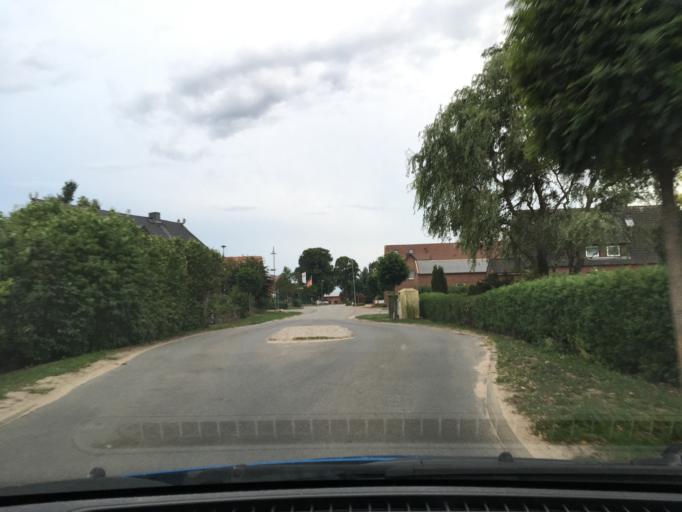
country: DE
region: Schleswig-Holstein
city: Lanze
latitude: 53.3879
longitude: 10.6052
